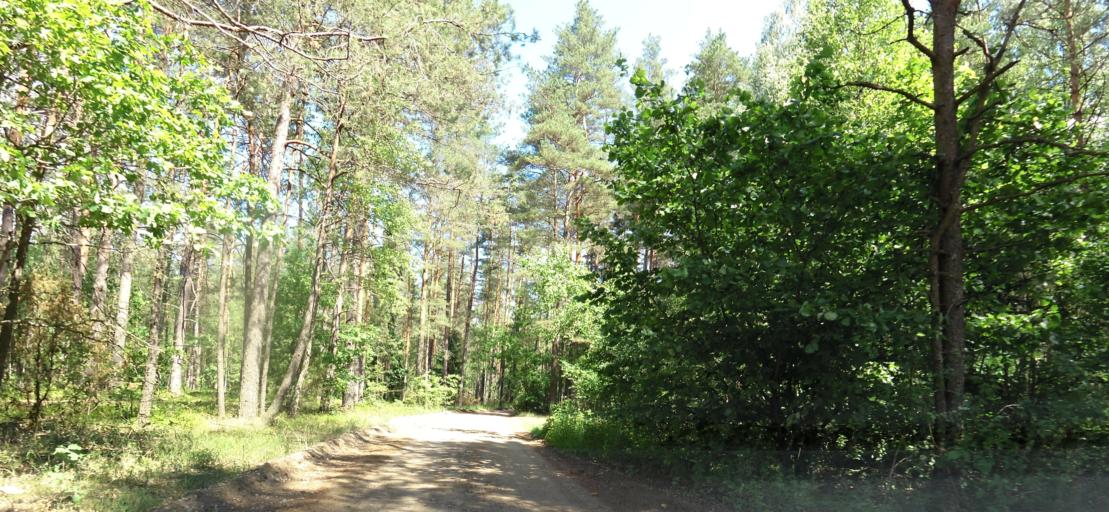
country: LT
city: Nemencine
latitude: 54.8157
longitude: 25.3885
